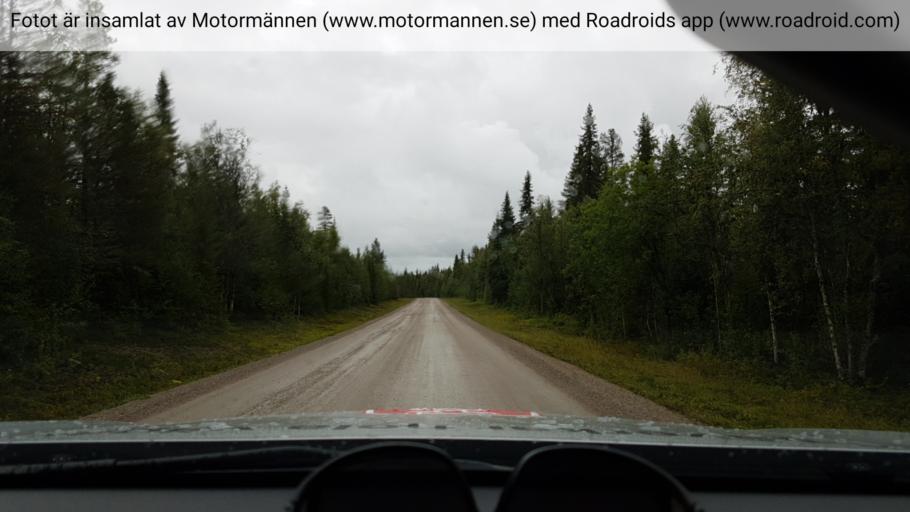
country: SE
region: Vaesterbotten
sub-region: Asele Kommun
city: Insjon
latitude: 64.7462
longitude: 17.6523
